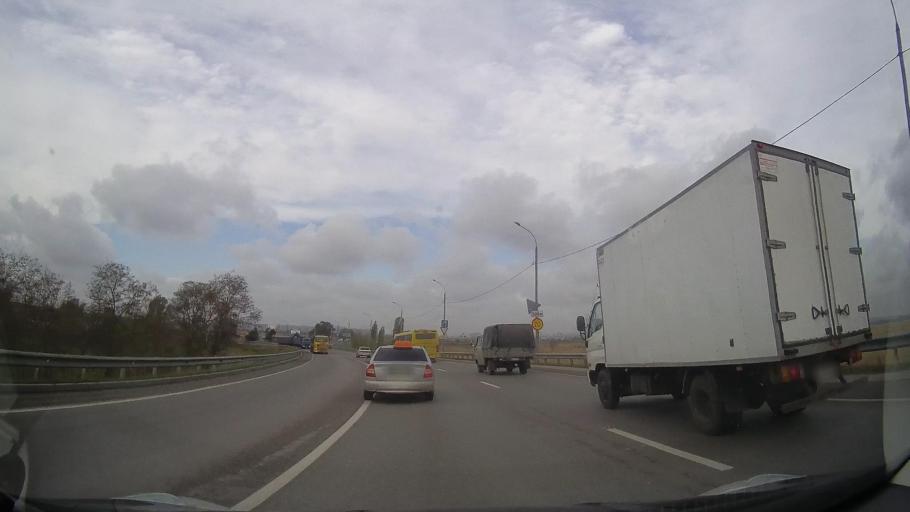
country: RU
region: Rostov
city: Bataysk
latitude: 47.1715
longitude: 39.7468
